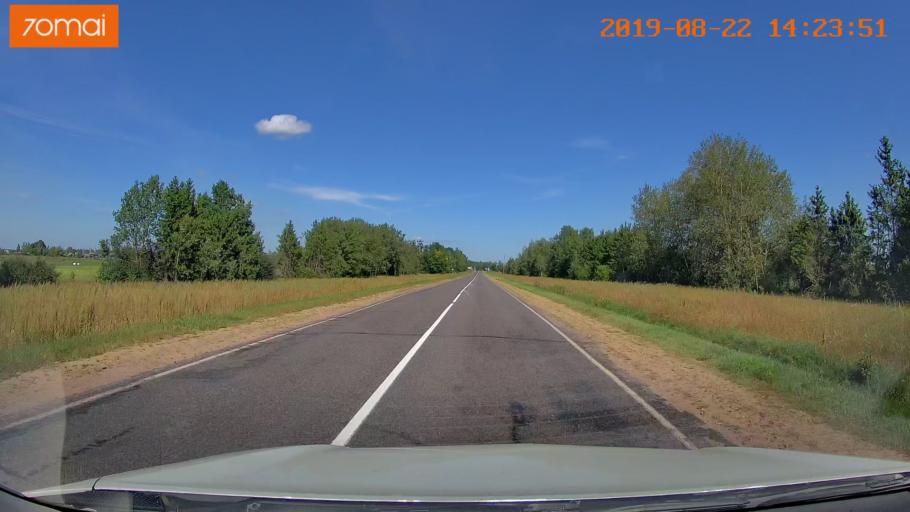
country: BY
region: Mogilev
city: Asipovichy
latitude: 53.2934
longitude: 28.5902
